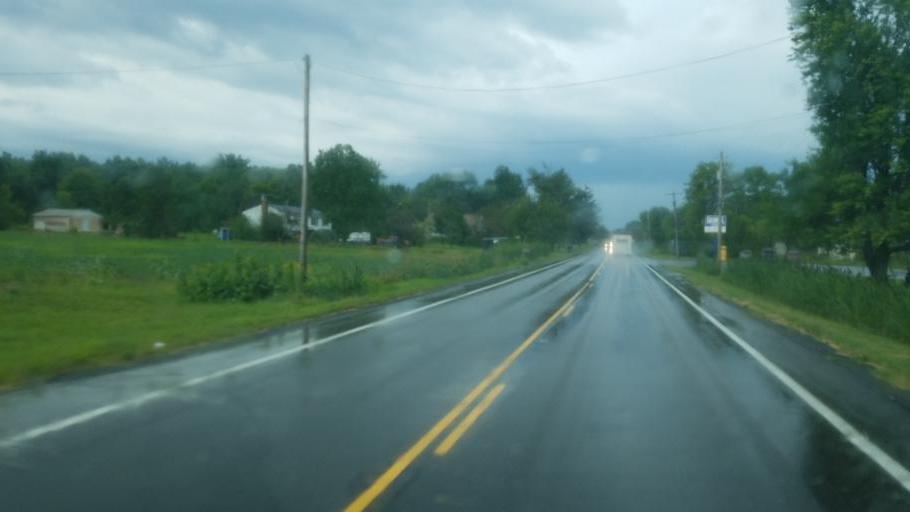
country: US
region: Ohio
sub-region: Trumbull County
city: Champion Heights
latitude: 41.3310
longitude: -80.8583
